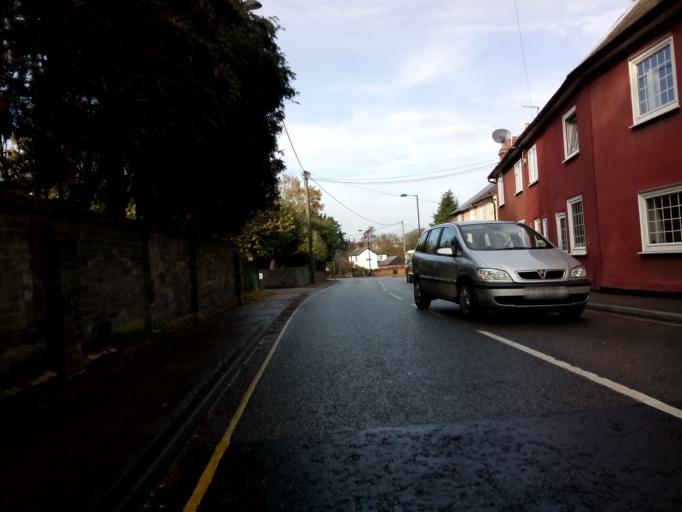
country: GB
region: England
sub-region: Suffolk
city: Needham Market
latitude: 52.1566
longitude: 1.0491
